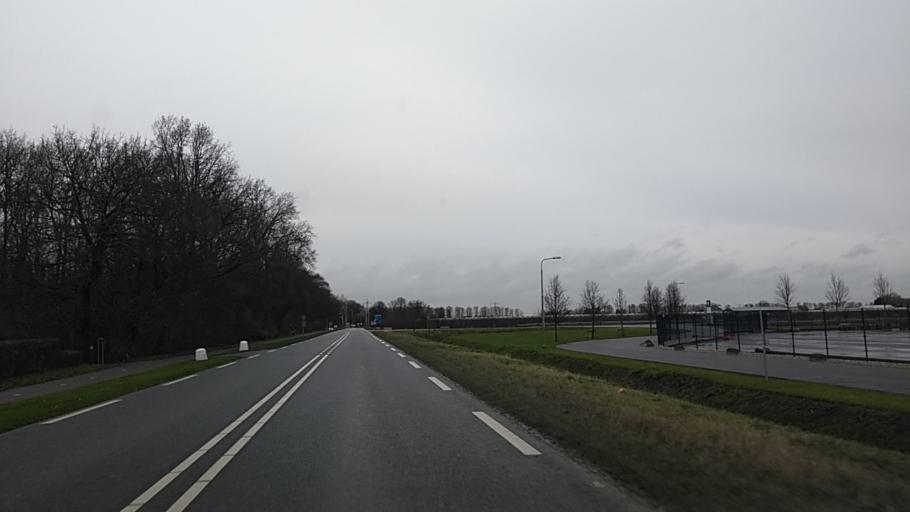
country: NL
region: Overijssel
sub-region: Gemeente Steenwijkerland
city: Blokzijl
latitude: 52.7392
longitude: 5.8580
